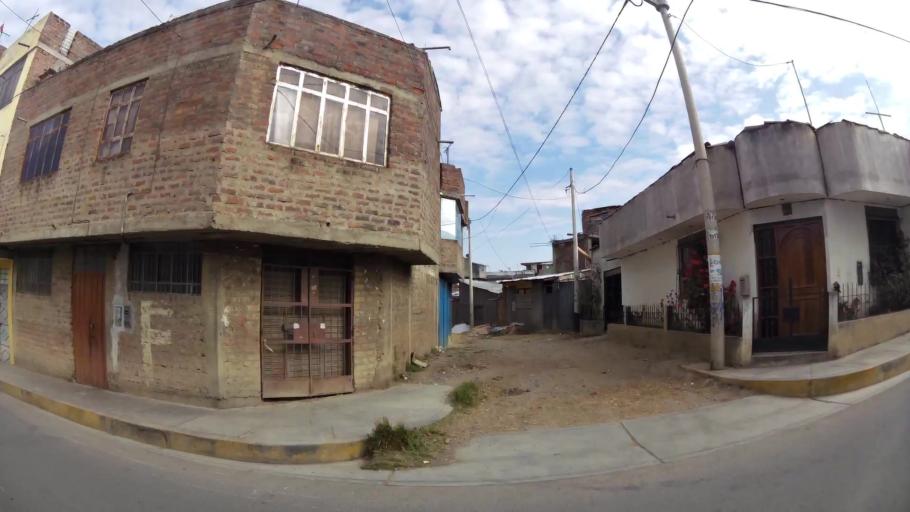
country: PE
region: Junin
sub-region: Provincia de Huancayo
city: Huancayo
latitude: -12.0606
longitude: -75.2020
